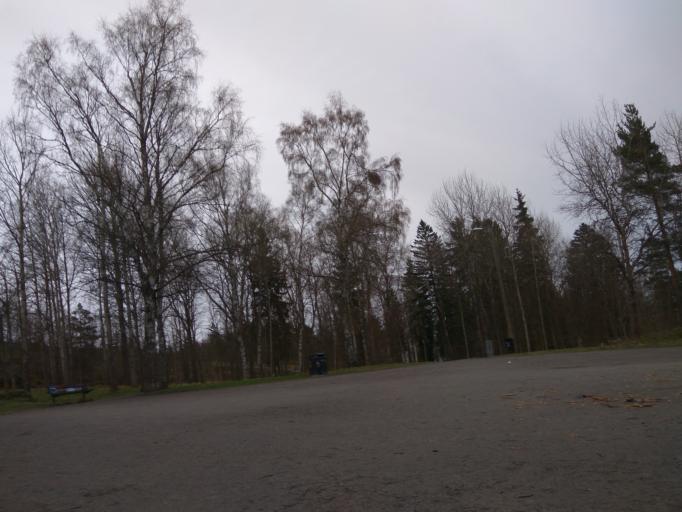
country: FI
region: Uusimaa
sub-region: Helsinki
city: Helsinki
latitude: 60.2188
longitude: 24.9529
